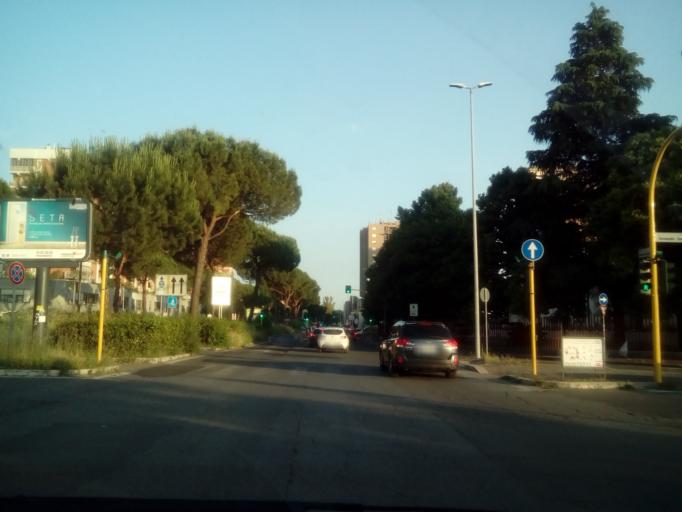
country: IT
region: Latium
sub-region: Citta metropolitana di Roma Capitale
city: Rome
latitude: 41.9140
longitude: 12.5700
